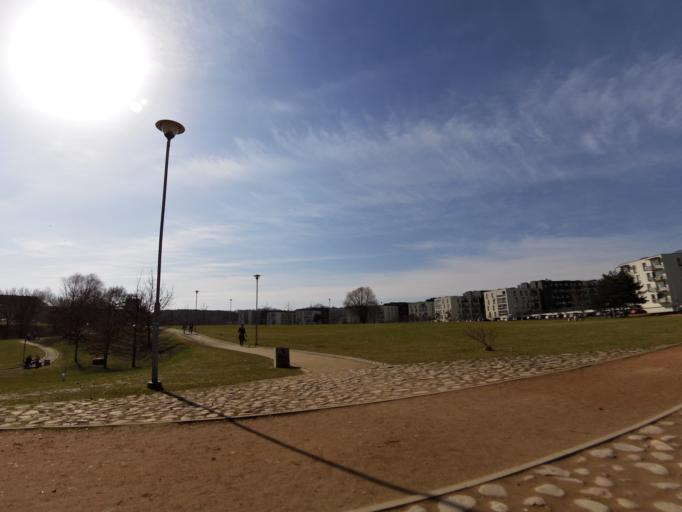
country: LT
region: Vilnius County
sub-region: Vilnius
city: Vilnius
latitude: 54.7186
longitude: 25.2812
